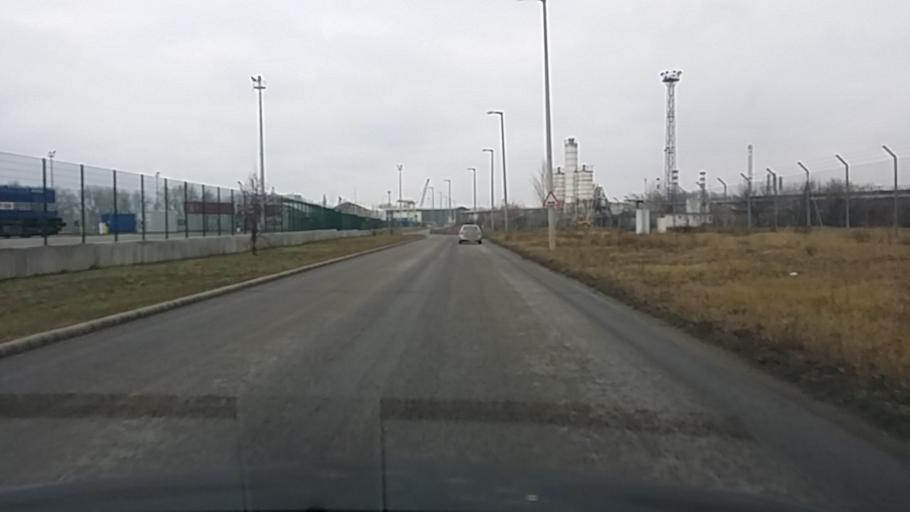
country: HU
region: Budapest
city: Budapest XXII. keruelet
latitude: 47.4182
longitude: 19.0516
